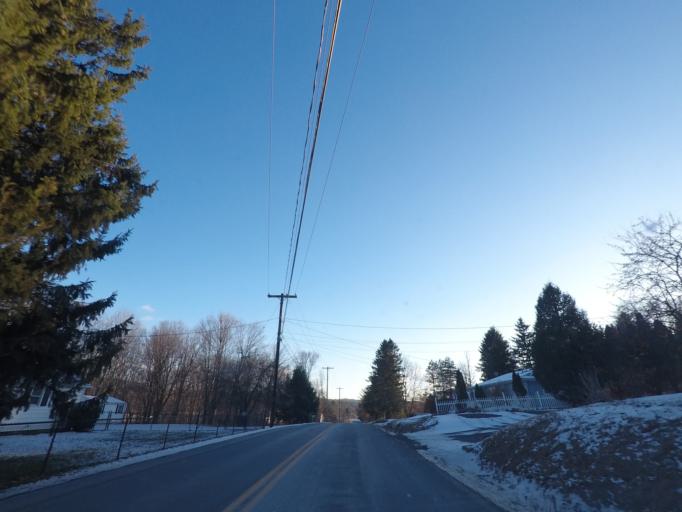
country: US
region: New York
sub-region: Rensselaer County
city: Poestenkill
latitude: 42.6990
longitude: -73.5807
